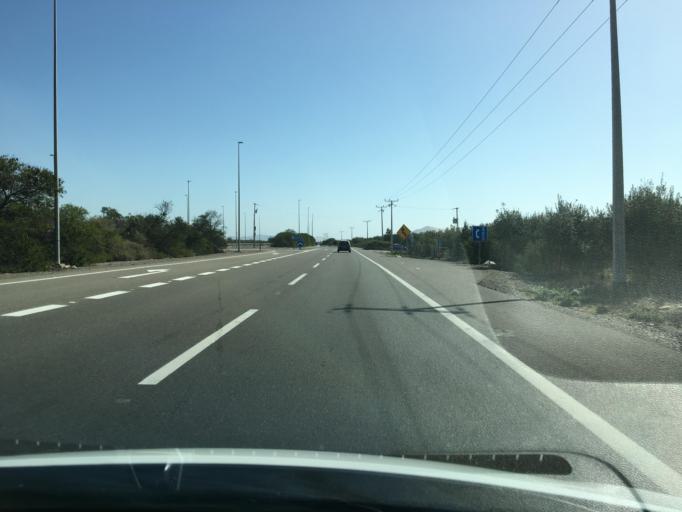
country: CL
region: Atacama
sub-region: Provincia de Copiapo
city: Copiapo
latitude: -27.3301
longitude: -70.5697
